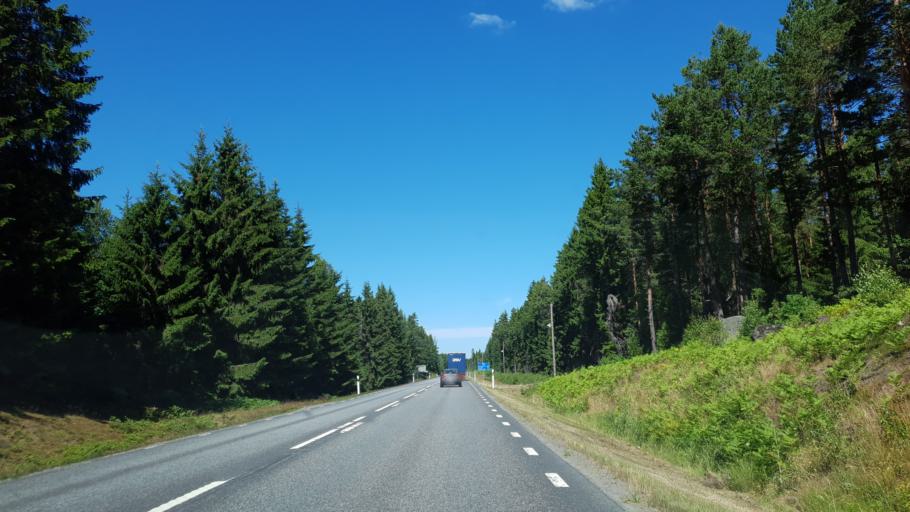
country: SE
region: Joenkoeping
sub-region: Varnamo Kommun
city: Rydaholm
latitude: 57.0336
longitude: 14.2498
